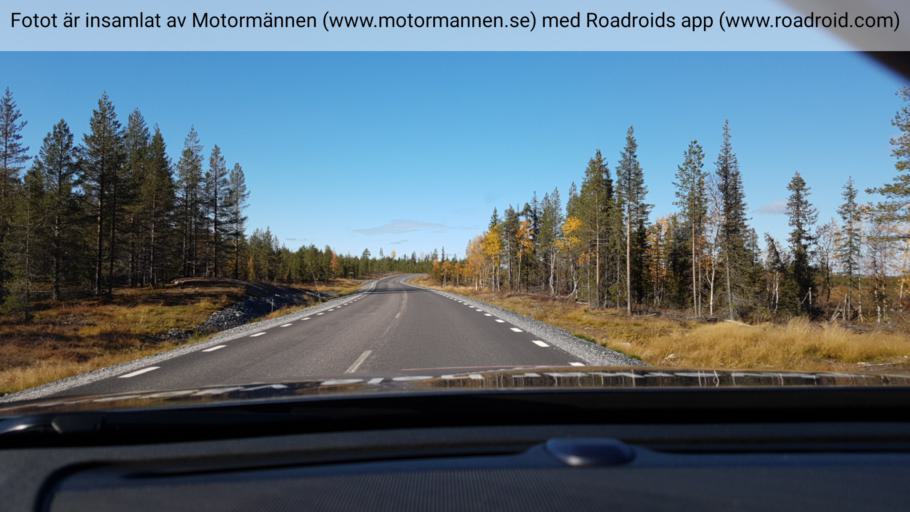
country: SE
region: Norrbotten
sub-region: Gallivare Kommun
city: Gaellivare
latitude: 66.8967
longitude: 20.9097
